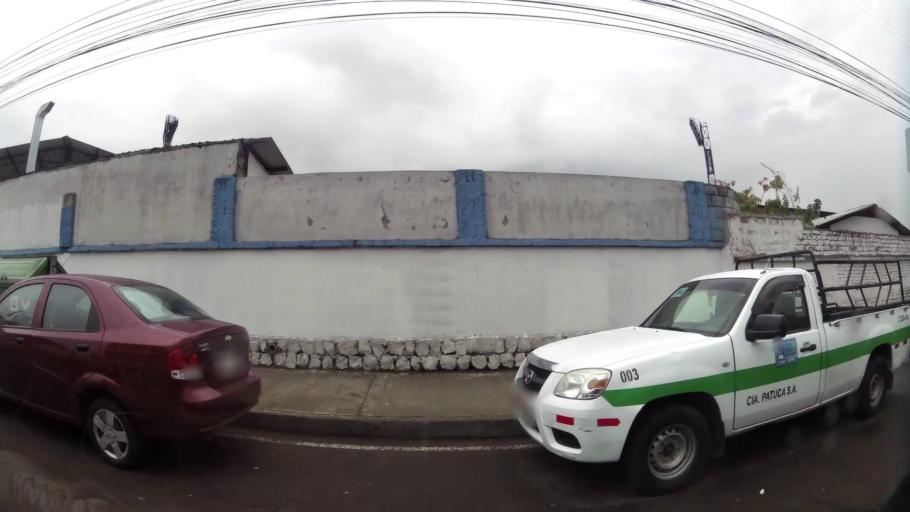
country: EC
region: Pichincha
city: Sangolqui
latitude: -0.3286
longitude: -78.4443
